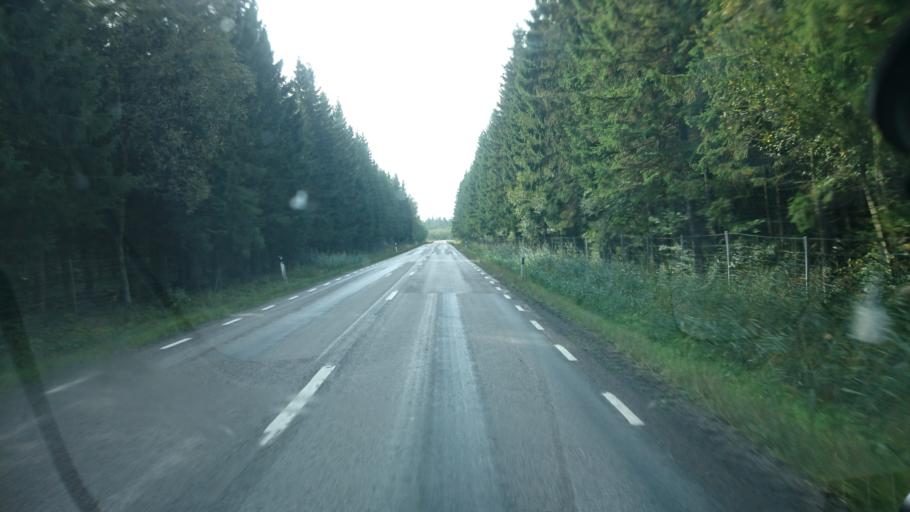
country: SE
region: Vaestra Goetaland
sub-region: Alingsas Kommun
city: Sollebrunn
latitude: 58.1856
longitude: 12.4249
